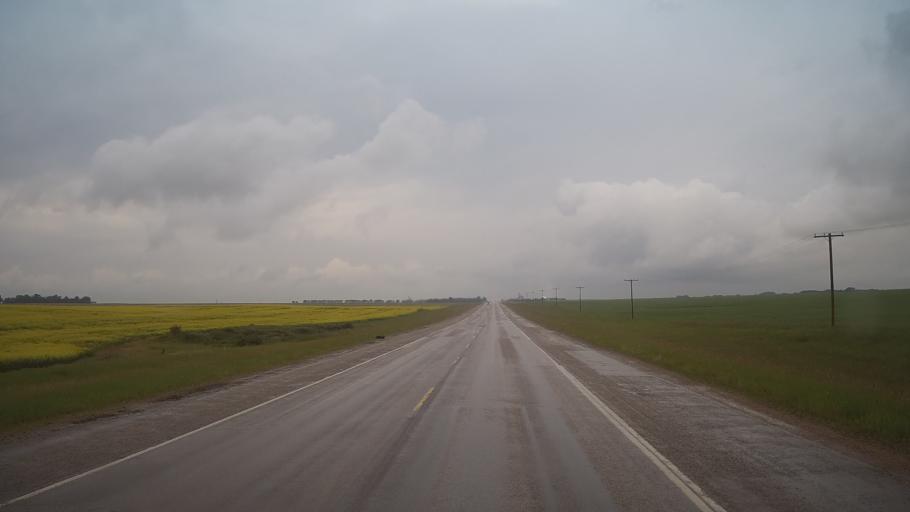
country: CA
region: Saskatchewan
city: Unity
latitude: 52.4350
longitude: -109.0549
